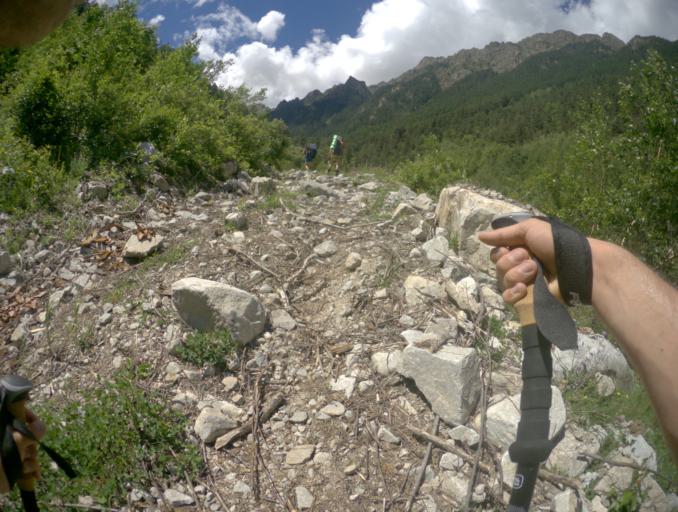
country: RU
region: Karachayevo-Cherkesiya
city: Uchkulan
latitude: 43.3543
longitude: 42.1747
